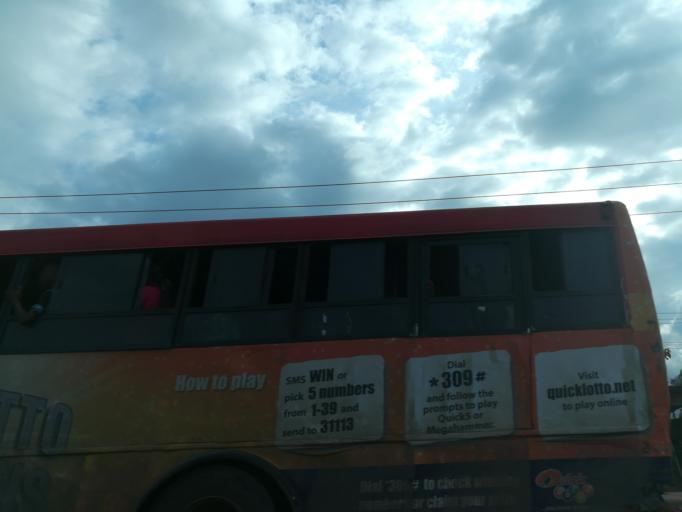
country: NG
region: Lagos
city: Ebute Ikorodu
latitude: 6.6146
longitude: 3.4760
